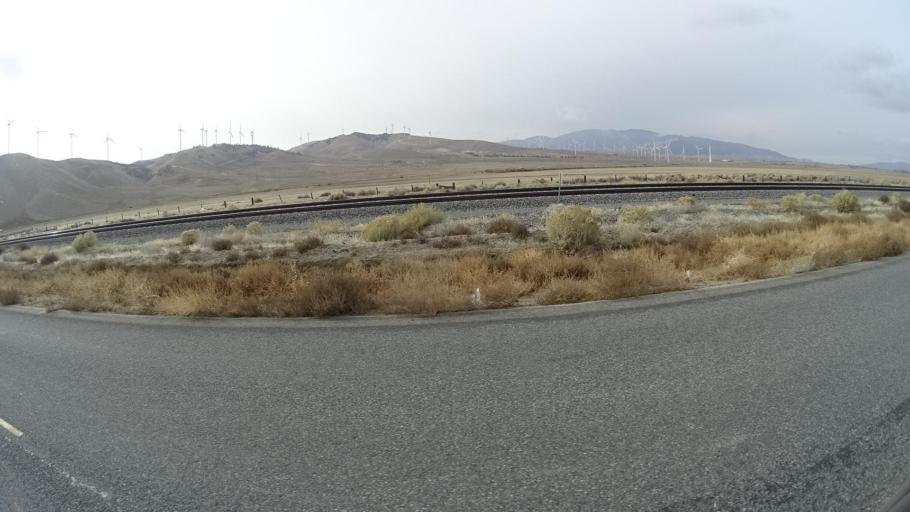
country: US
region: California
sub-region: Kern County
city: Tehachapi
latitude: 35.1172
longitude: -118.3370
